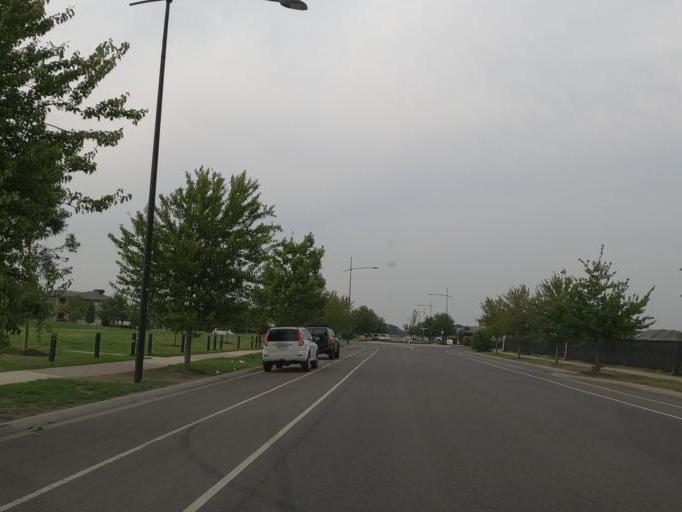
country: AU
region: Victoria
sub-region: Hume
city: Greenvale
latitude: -37.6231
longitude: 144.8785
